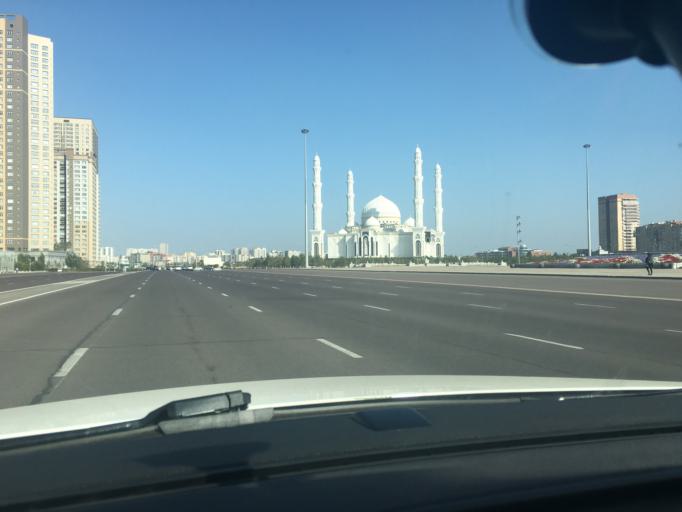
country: KZ
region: Astana Qalasy
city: Astana
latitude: 51.1219
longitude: 71.4681
